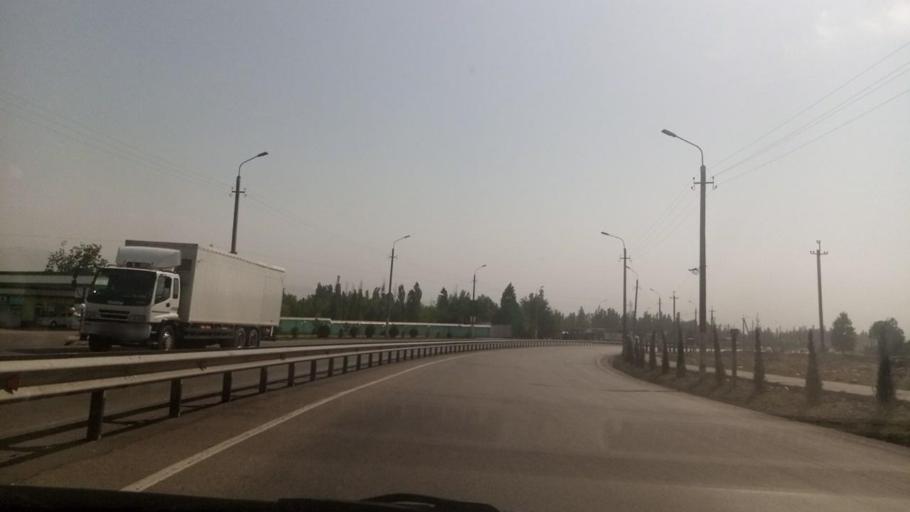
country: UZ
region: Toshkent
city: Angren
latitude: 41.0270
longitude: 70.1363
